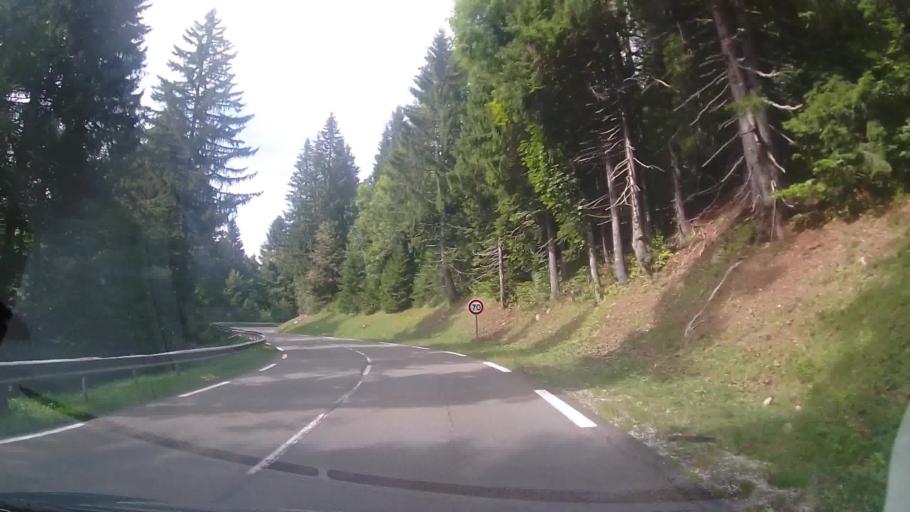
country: FR
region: Franche-Comte
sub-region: Departement du Jura
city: Les Rousses
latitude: 46.4126
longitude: 6.0622
